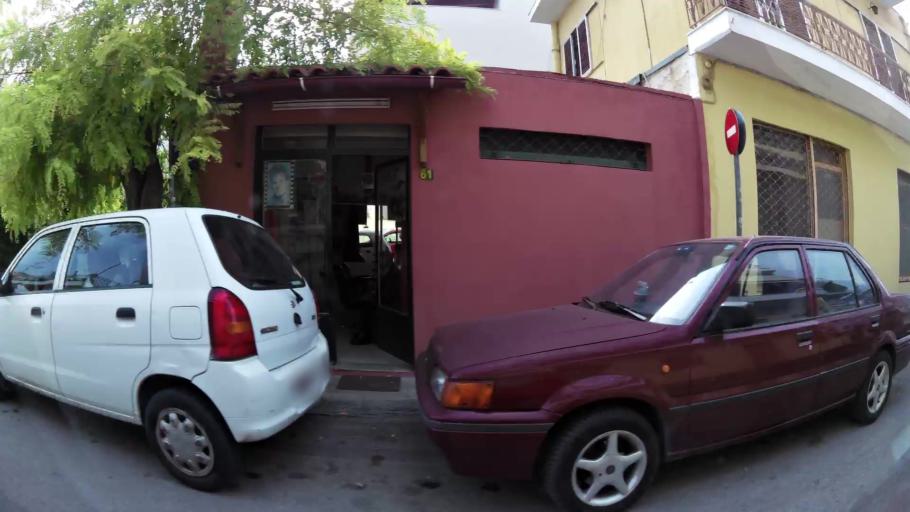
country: GR
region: Attica
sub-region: Nomarchia Athinas
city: Petroupolis
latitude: 38.0269
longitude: 23.6761
